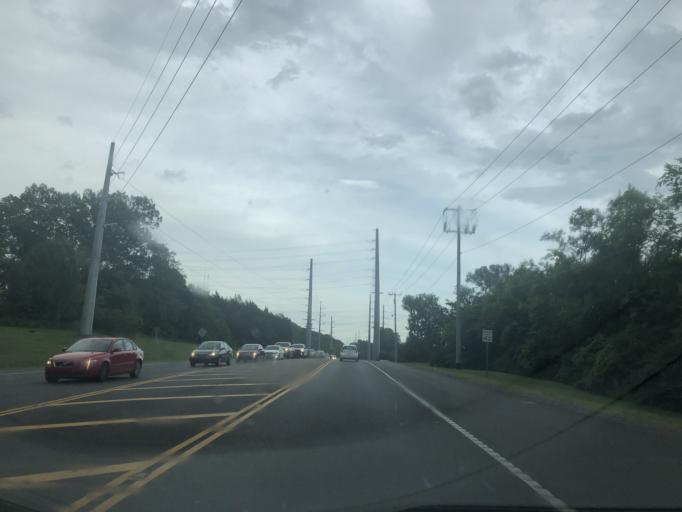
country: US
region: Tennessee
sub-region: Davidson County
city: Forest Hills
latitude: 36.0470
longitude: -86.8615
